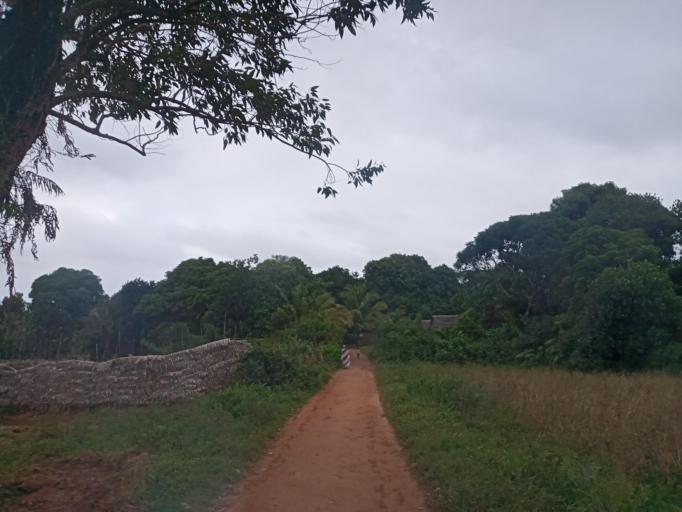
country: MG
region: Atsimo-Atsinanana
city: Vohipaho
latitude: -24.0422
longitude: 47.4401
